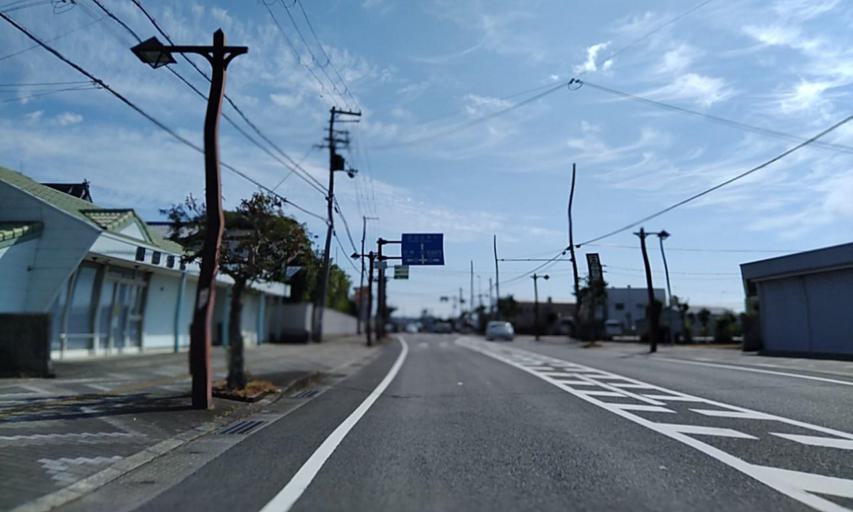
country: JP
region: Wakayama
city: Gobo
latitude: 33.9020
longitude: 135.1616
